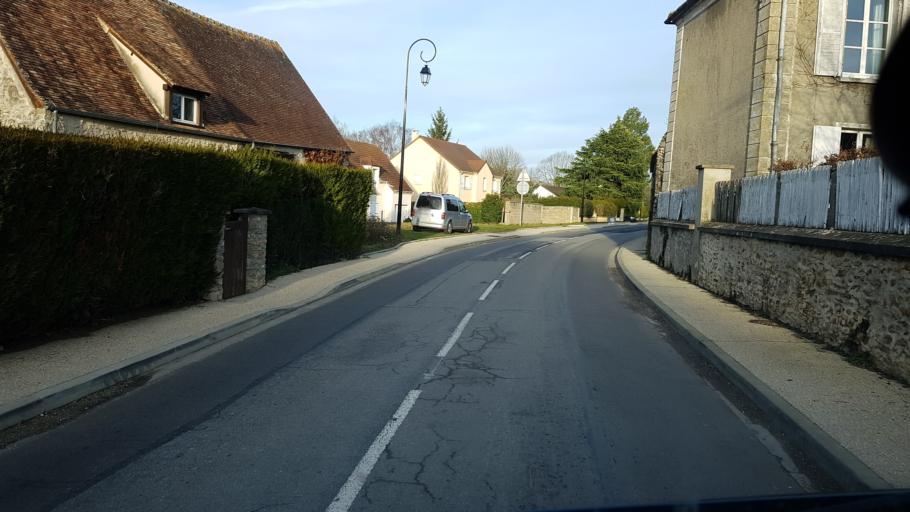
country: FR
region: Ile-de-France
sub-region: Departement des Yvelines
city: Gazeran
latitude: 48.6730
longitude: 1.7489
